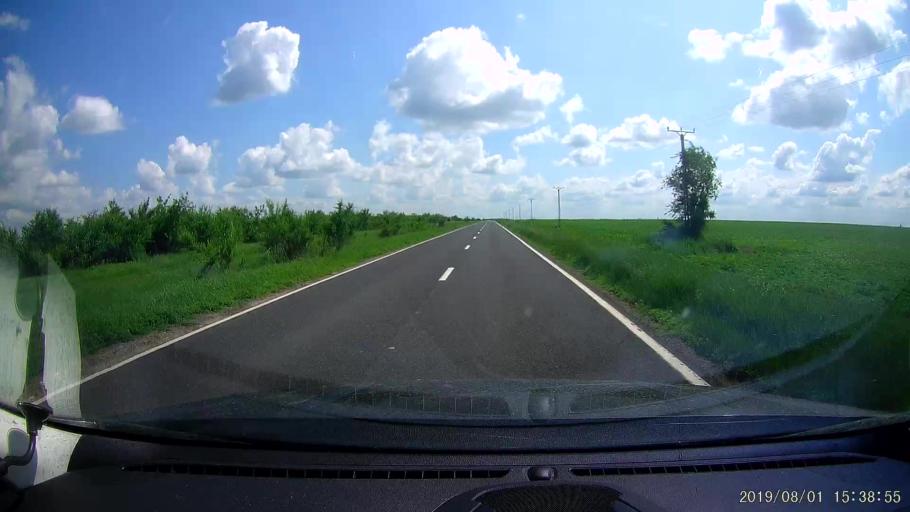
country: RO
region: Braila
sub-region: Comuna Insuratei
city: Insuratei
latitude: 44.8700
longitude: 27.5689
